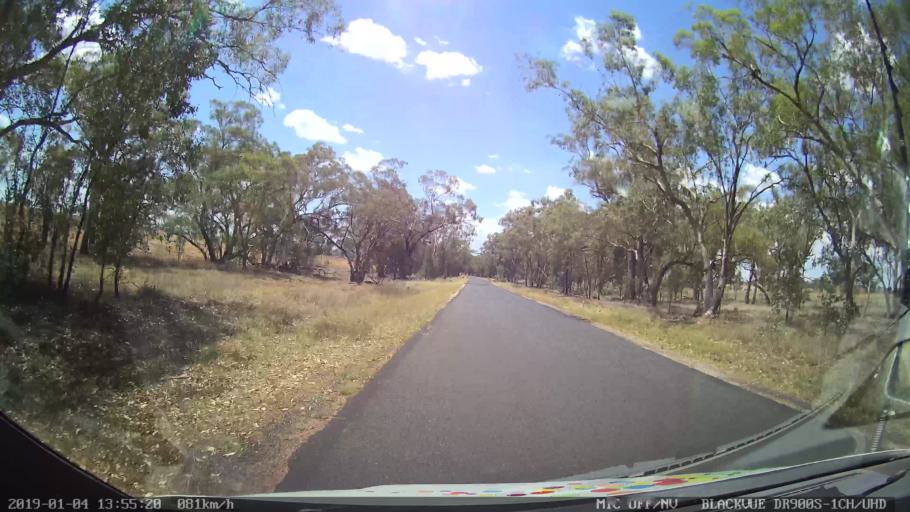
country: AU
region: New South Wales
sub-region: Dubbo Municipality
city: Dubbo
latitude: -32.3631
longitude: 148.5864
